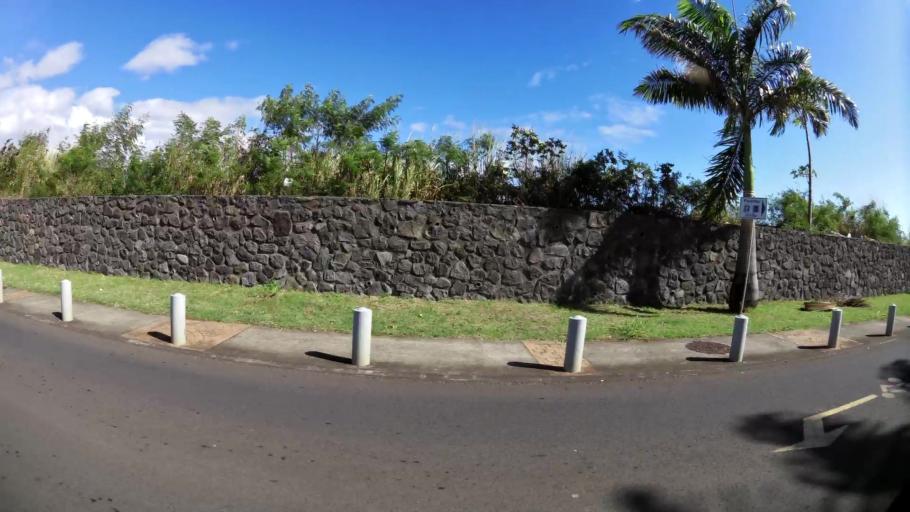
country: RE
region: Reunion
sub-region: Reunion
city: Sainte-Marie
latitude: -20.8954
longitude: 55.4999
